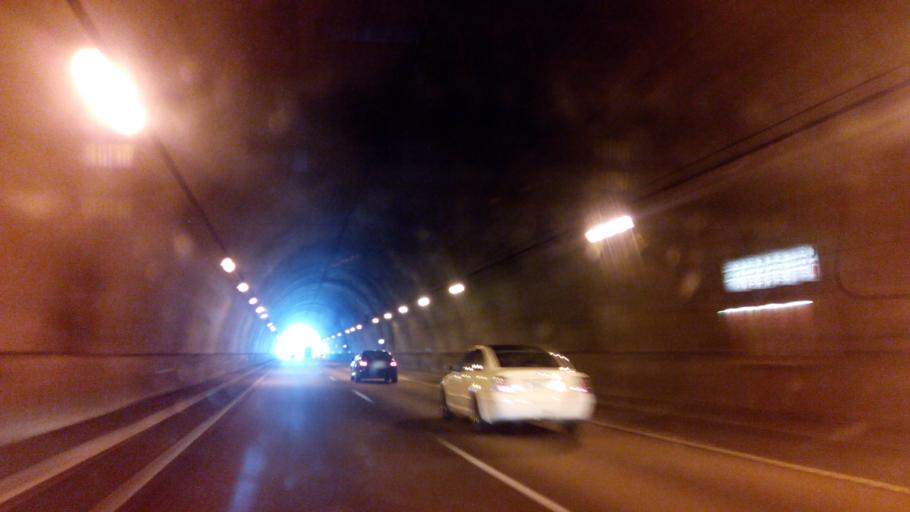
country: ES
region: Galicia
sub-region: Provincia de Pontevedra
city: Vigo
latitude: 42.2526
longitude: -8.6787
